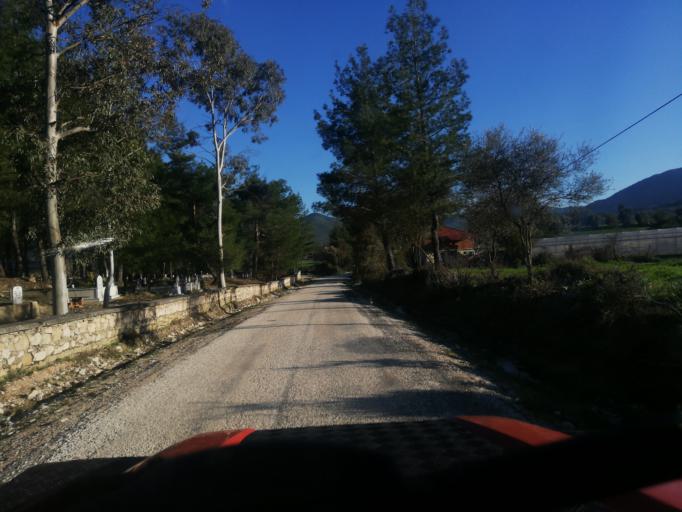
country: TR
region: Antalya
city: Kas
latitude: 36.2849
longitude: 29.7061
